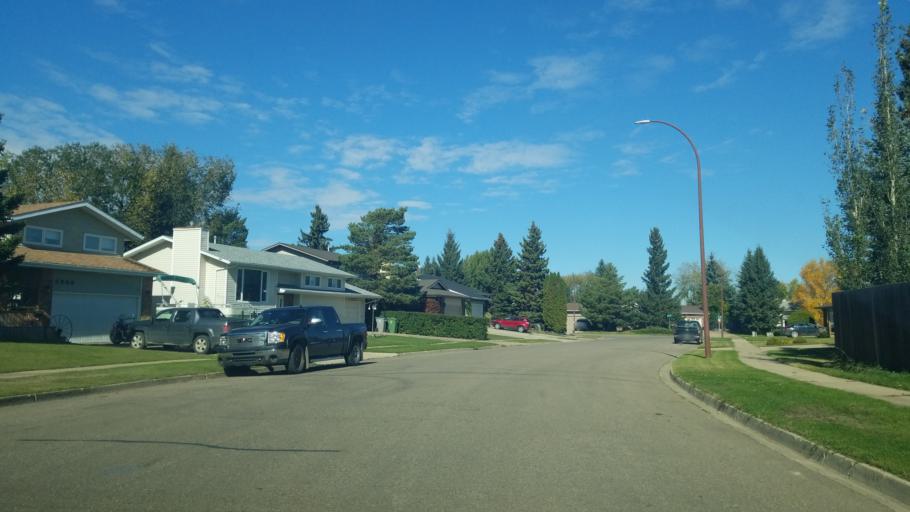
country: CA
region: Saskatchewan
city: Lloydminster
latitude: 53.2720
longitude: -110.0146
